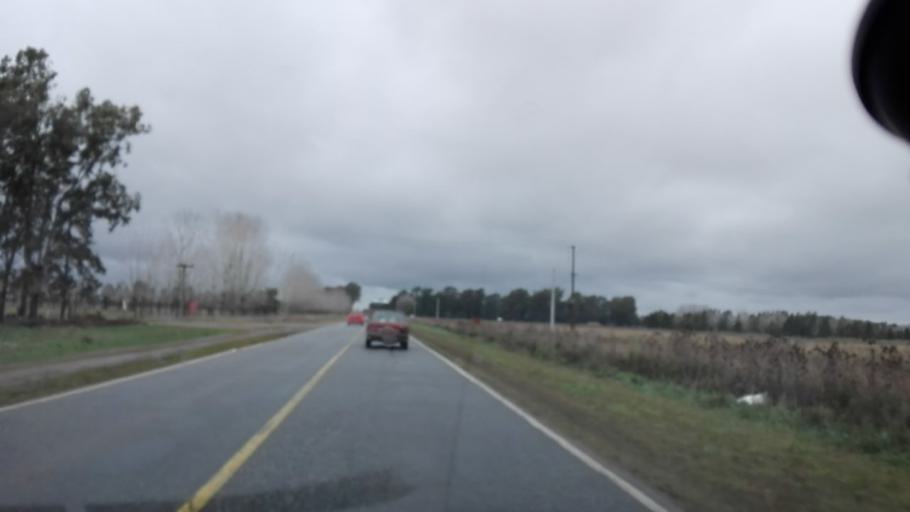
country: AR
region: Buenos Aires
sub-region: Partido de Brandsen
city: Brandsen
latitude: -35.1776
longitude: -58.2966
